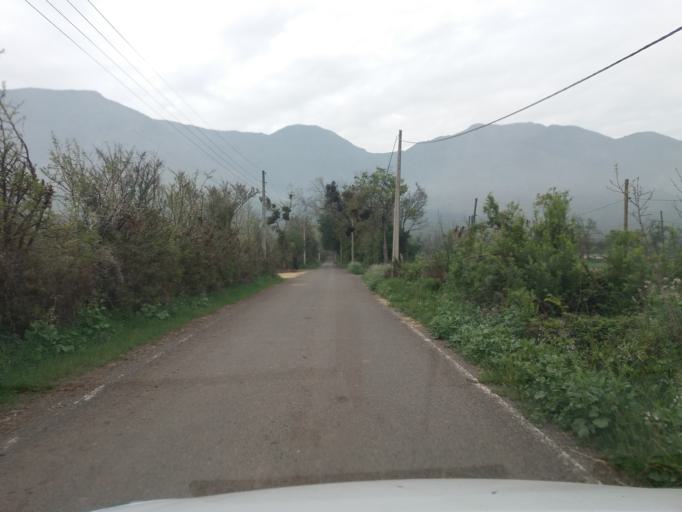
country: CL
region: Valparaiso
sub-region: Provincia de San Felipe
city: Llaillay
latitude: -32.8459
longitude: -71.0633
